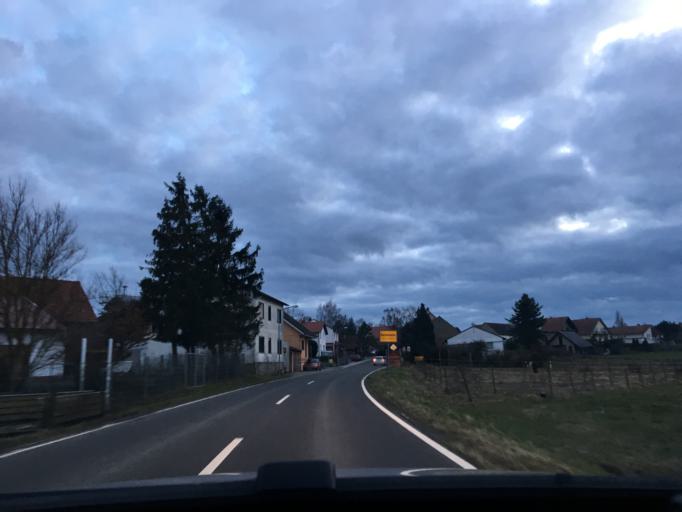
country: DE
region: Rheinland-Pfalz
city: Bechenheim
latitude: 49.7301
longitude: 8.0030
